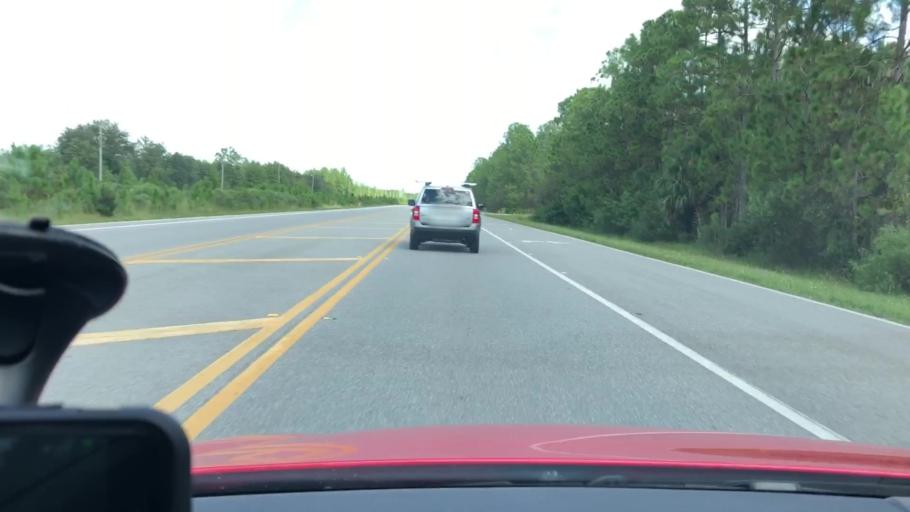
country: US
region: Florida
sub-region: Volusia County
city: Holly Hill
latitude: 29.1989
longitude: -81.1198
